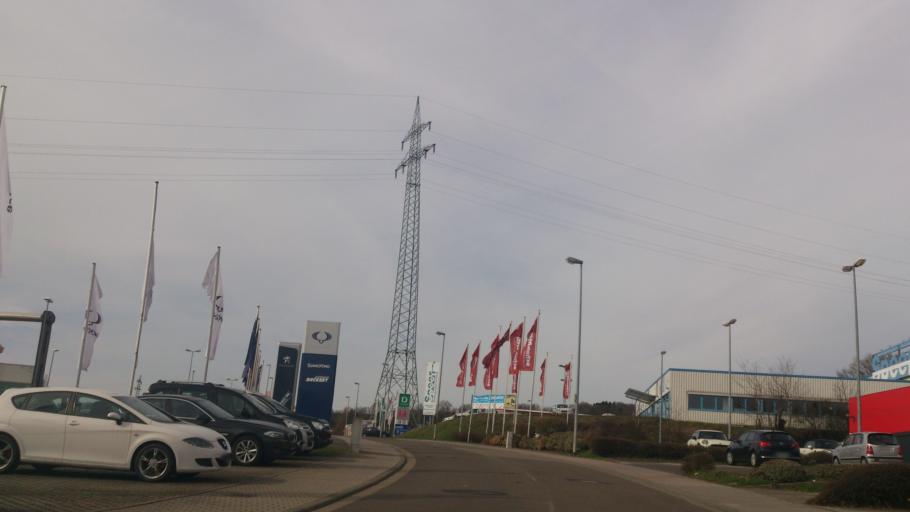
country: DE
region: Rheinland-Pfalz
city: Zweibrucken
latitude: 49.2601
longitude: 7.3387
